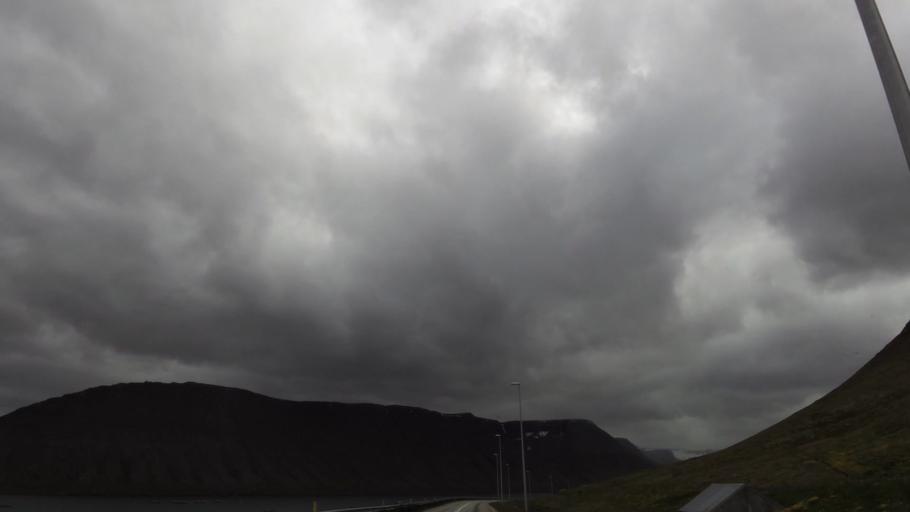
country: IS
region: Westfjords
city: Isafjoerdur
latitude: 66.1013
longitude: -23.1096
